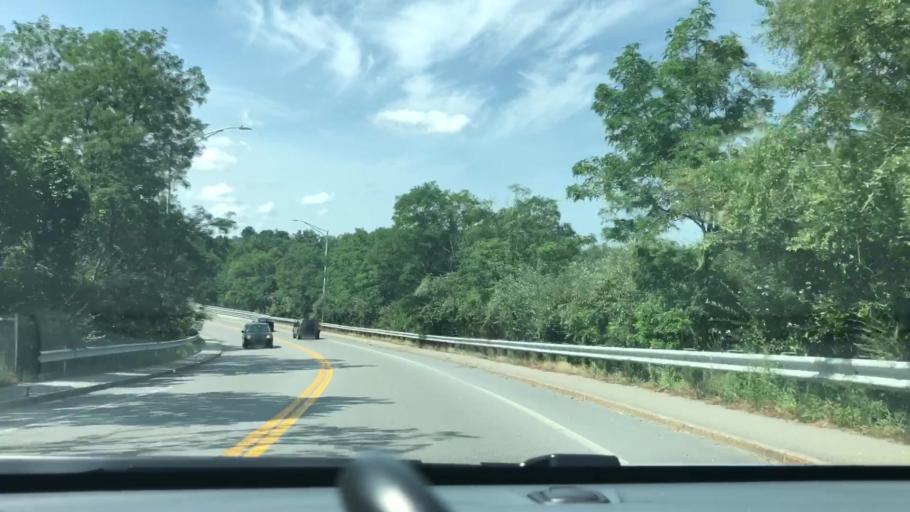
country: US
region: New Hampshire
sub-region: Hillsborough County
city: Pinardville
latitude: 42.9948
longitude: -71.4925
